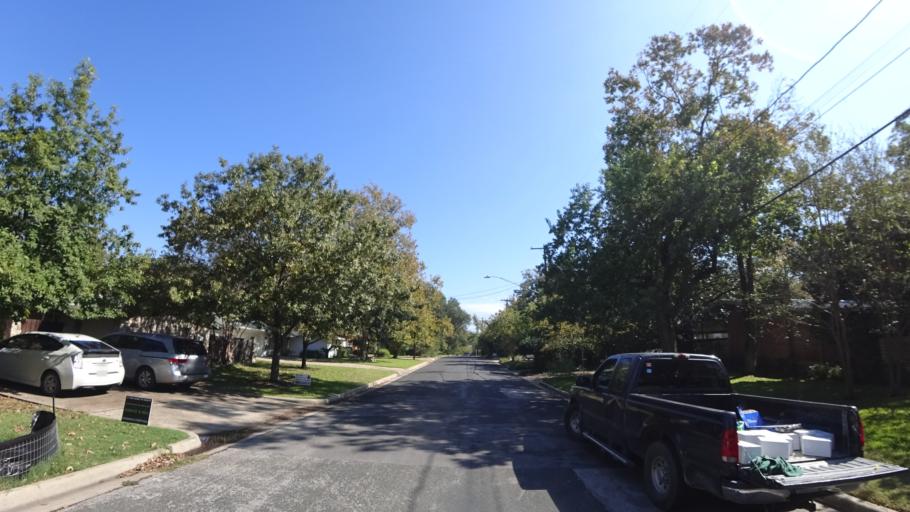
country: US
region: Texas
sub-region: Travis County
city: Austin
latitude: 30.2585
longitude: -97.7681
